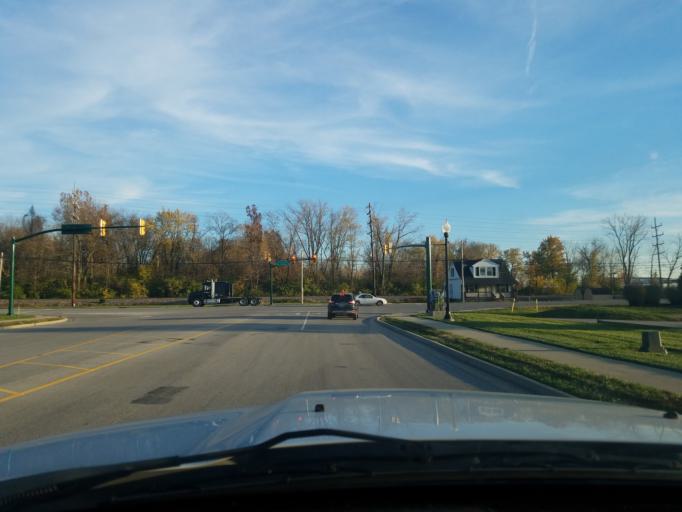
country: US
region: Indiana
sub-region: Clark County
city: Clarksville
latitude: 38.3222
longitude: -85.7486
